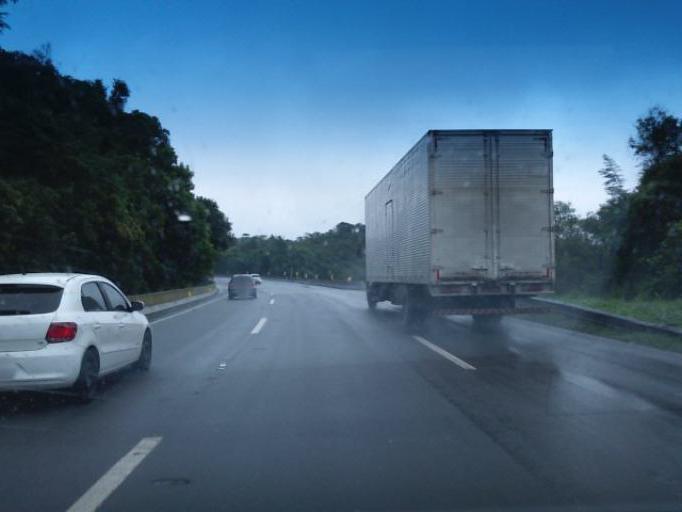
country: BR
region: Parana
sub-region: Sao Jose Dos Pinhais
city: Sao Jose dos Pinhais
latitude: -25.8402
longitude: -49.0368
